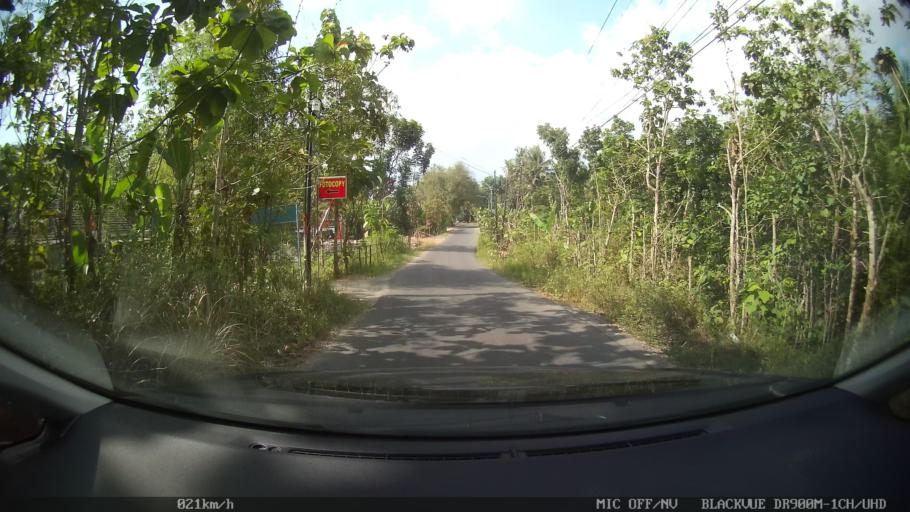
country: ID
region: Daerah Istimewa Yogyakarta
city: Kasihan
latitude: -7.8445
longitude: 110.3028
